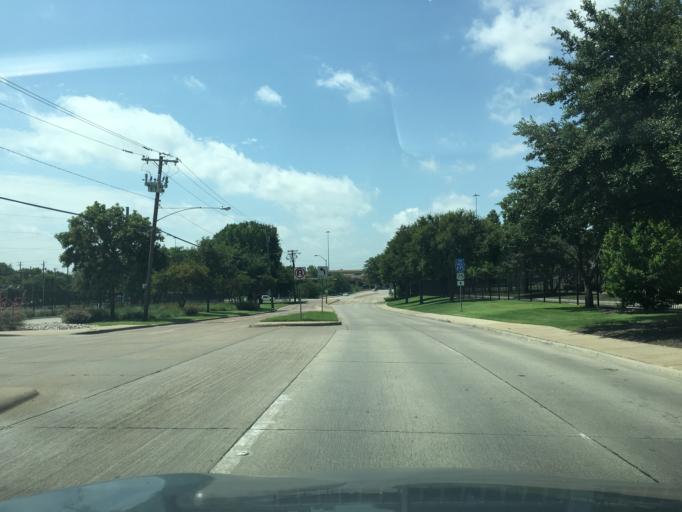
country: US
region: Texas
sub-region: Dallas County
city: Richardson
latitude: 32.9248
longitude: -96.7495
